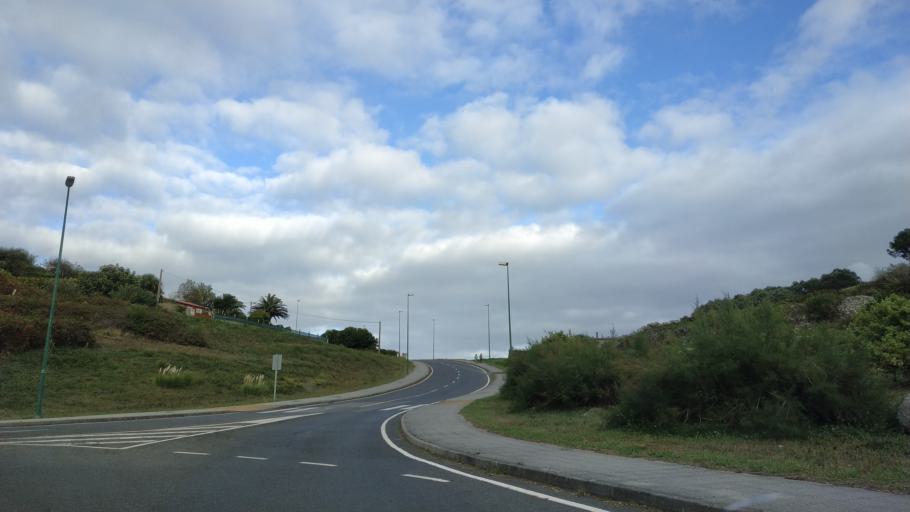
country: ES
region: Galicia
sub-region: Provincia da Coruna
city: A Coruna
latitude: 43.3704
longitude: -8.4434
